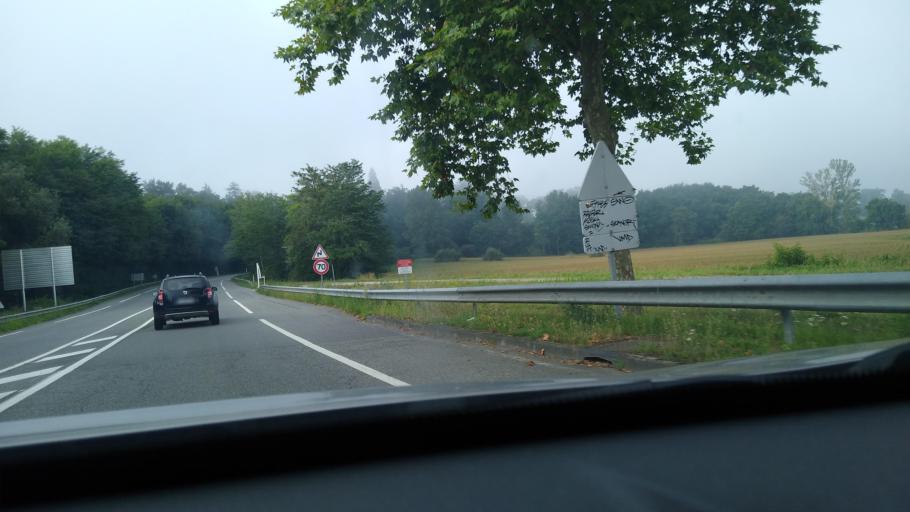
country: FR
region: Midi-Pyrenees
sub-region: Departement de la Haute-Garonne
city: Salies-du-Salat
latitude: 43.1225
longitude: 0.9357
